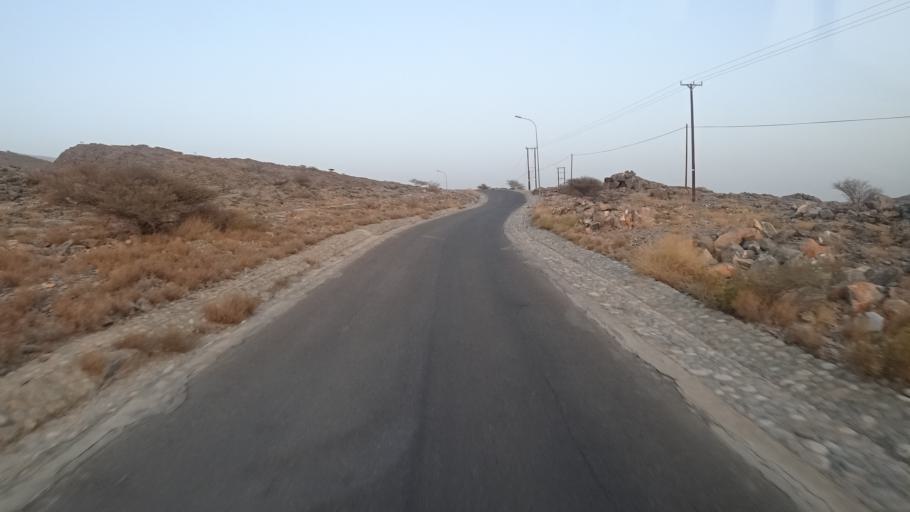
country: OM
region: Muhafazat ad Dakhiliyah
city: Bahla'
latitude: 23.1290
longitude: 57.3041
